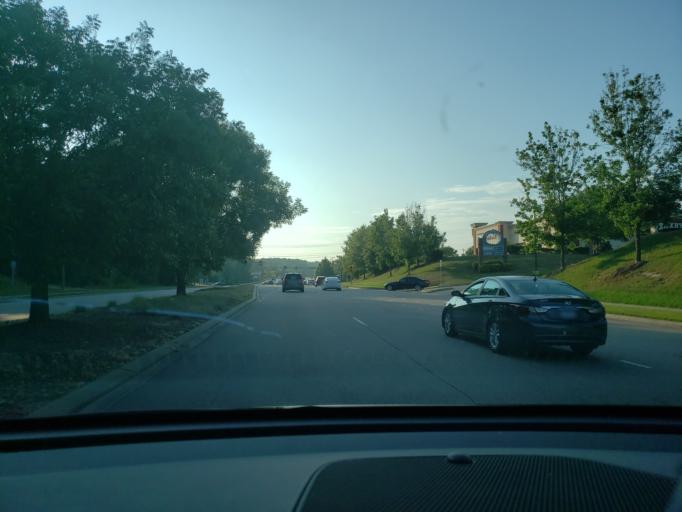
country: US
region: North Carolina
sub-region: Durham County
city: Durham
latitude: 35.9468
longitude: -78.9226
